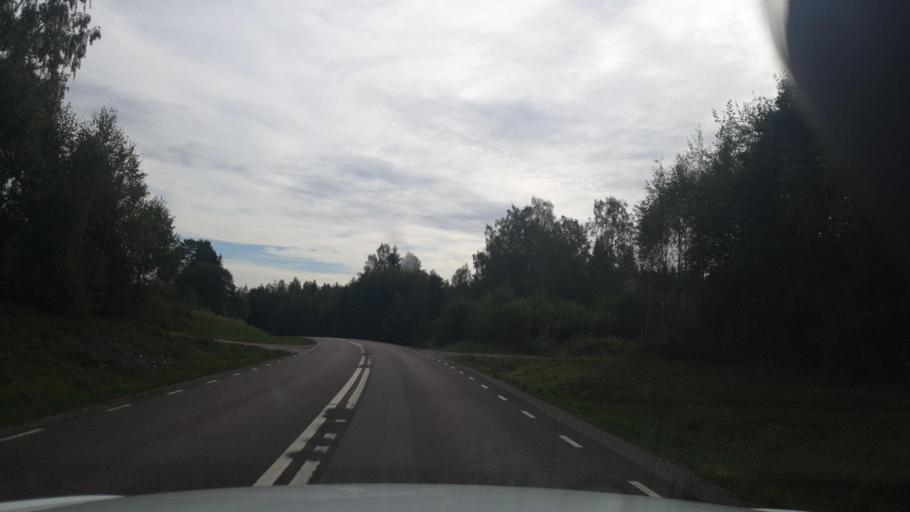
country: SE
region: Vaermland
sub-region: Eda Kommun
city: Amotfors
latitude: 59.6744
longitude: 12.4507
